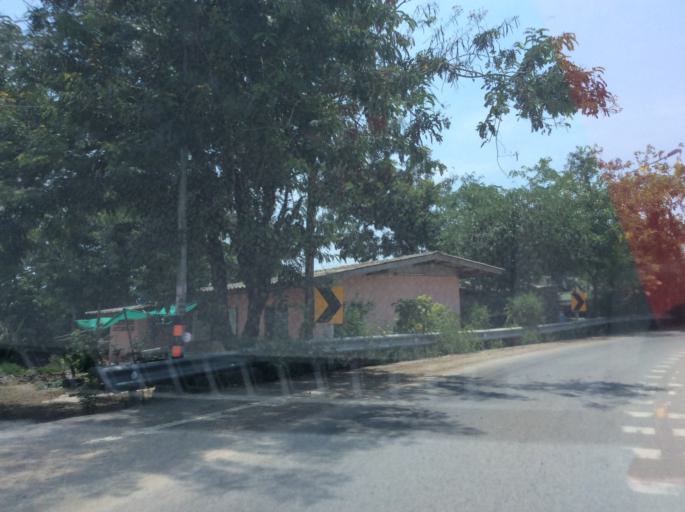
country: TH
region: Pathum Thani
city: Ban Rangsit
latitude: 14.0192
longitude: 100.7785
